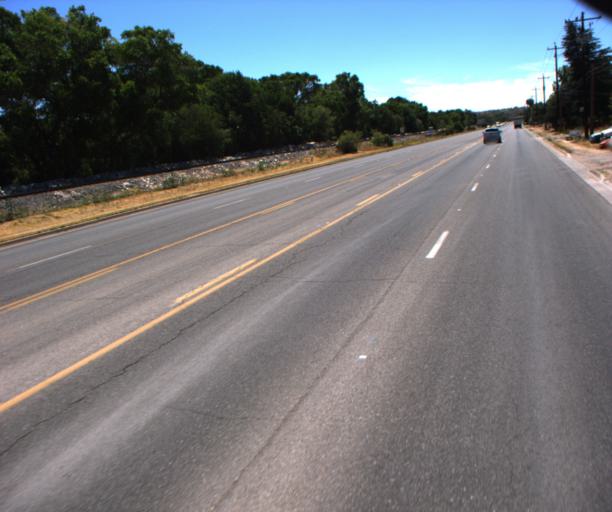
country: US
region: Arizona
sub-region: Santa Cruz County
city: Nogales
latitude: 31.3764
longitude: -110.9384
